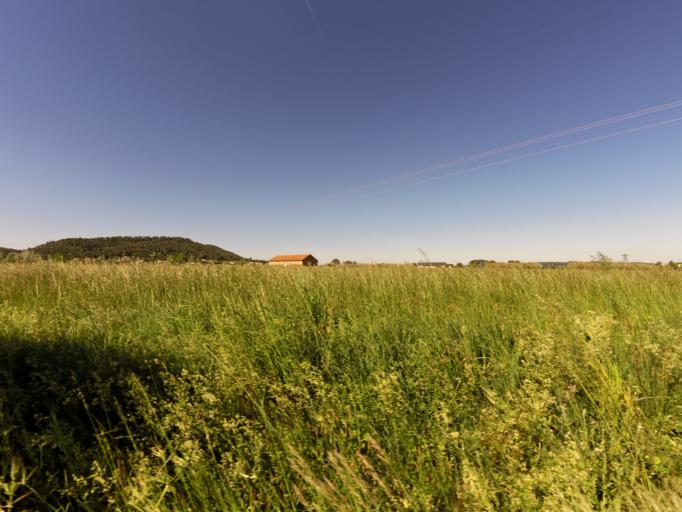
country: FR
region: Languedoc-Roussillon
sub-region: Departement du Gard
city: Sommieres
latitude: 43.8314
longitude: 4.0297
